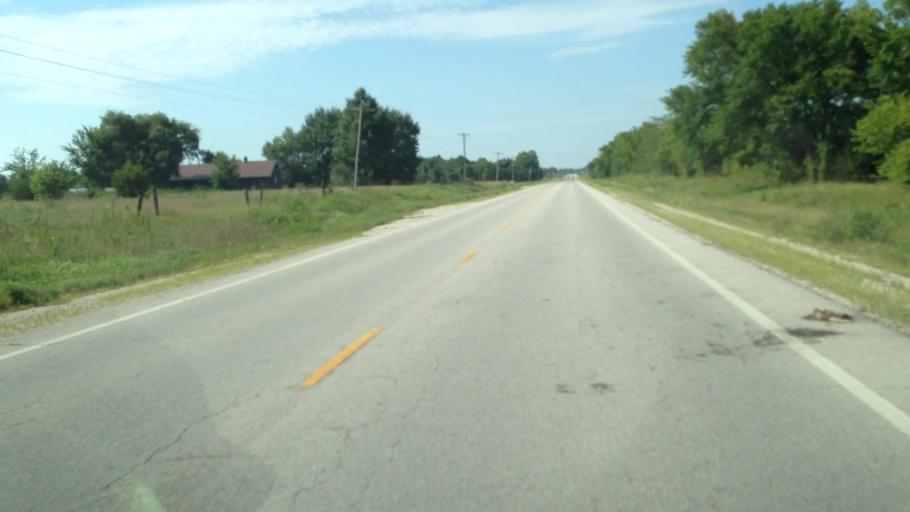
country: US
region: Kansas
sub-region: Neosho County
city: Erie
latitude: 37.5074
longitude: -95.2698
